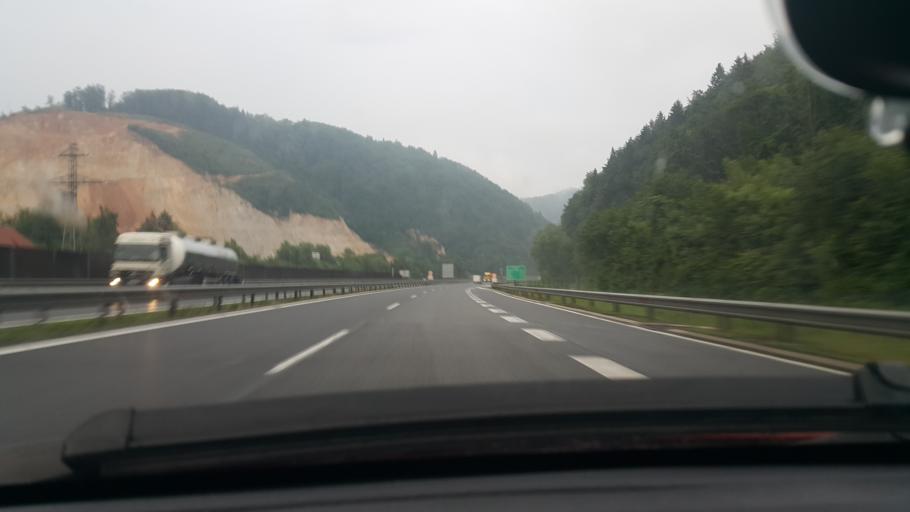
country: SI
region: Lukovica
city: Lukovica pri Domzalah
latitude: 46.1702
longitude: 14.6990
